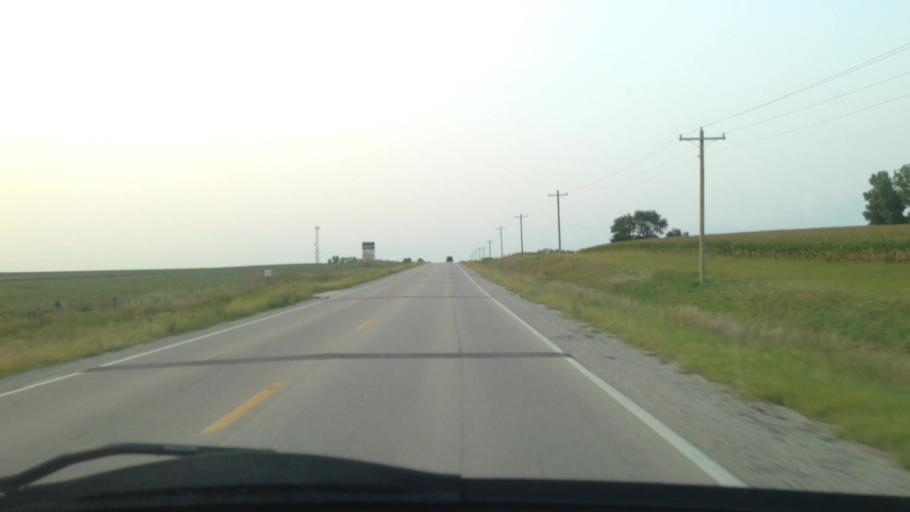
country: US
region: Iowa
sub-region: Linn County
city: Palo
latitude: 42.0707
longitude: -91.8691
